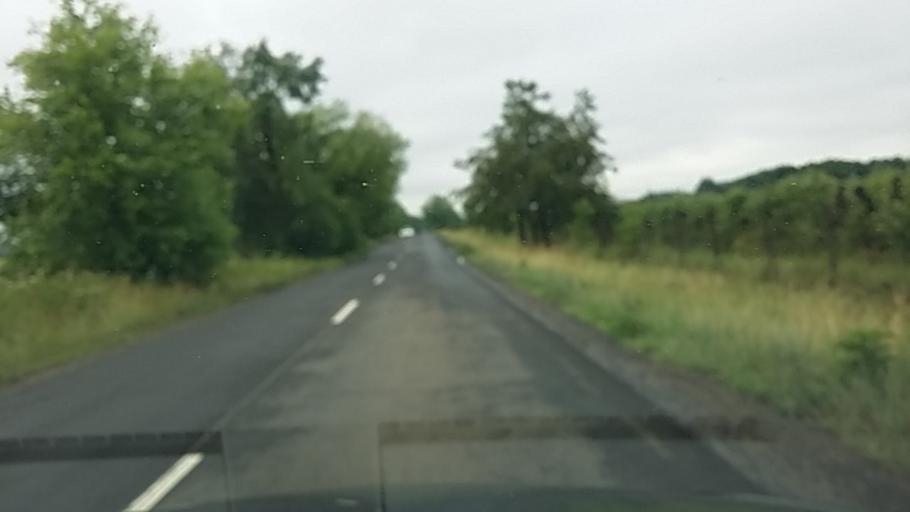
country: SK
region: Nitriansky
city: Zeliezovce
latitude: 47.9686
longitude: 18.7826
